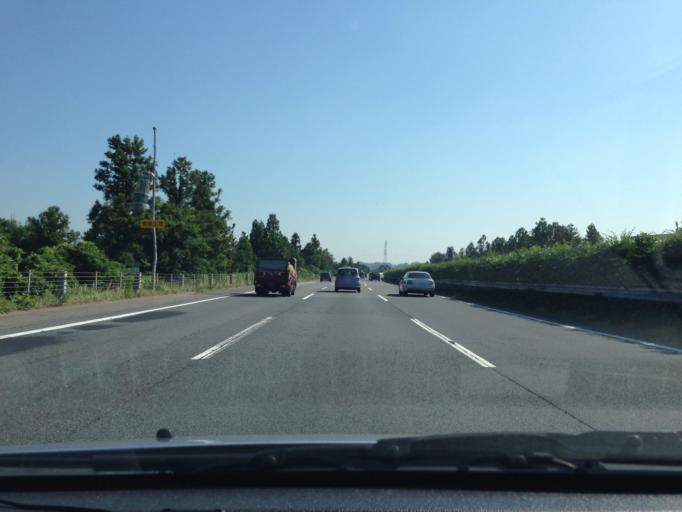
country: JP
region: Ibaraki
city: Naka
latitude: 36.0884
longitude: 140.1578
